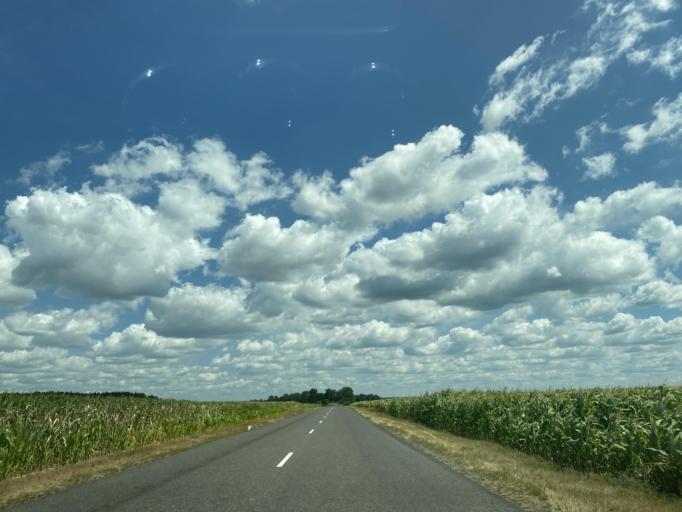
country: BY
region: Brest
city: Ivanava
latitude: 52.1748
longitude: 25.5780
